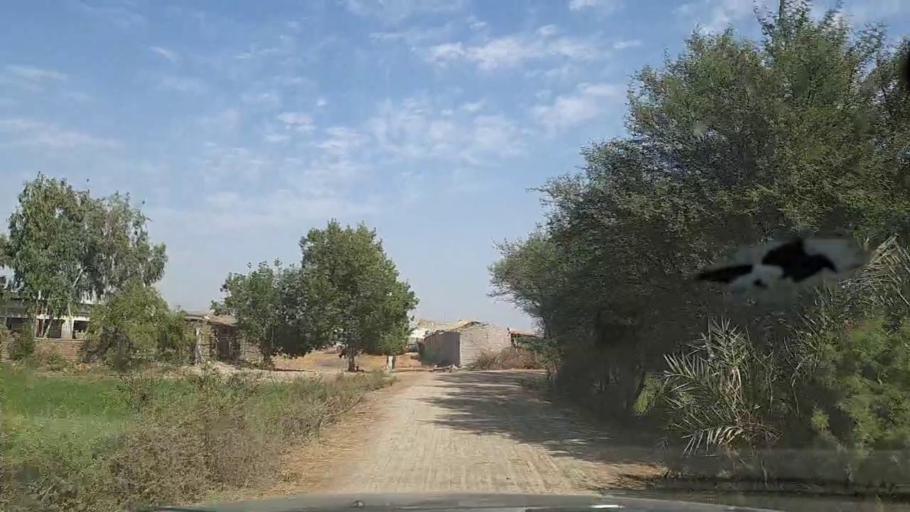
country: PK
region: Sindh
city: Daro Mehar
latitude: 24.6618
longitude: 68.0846
